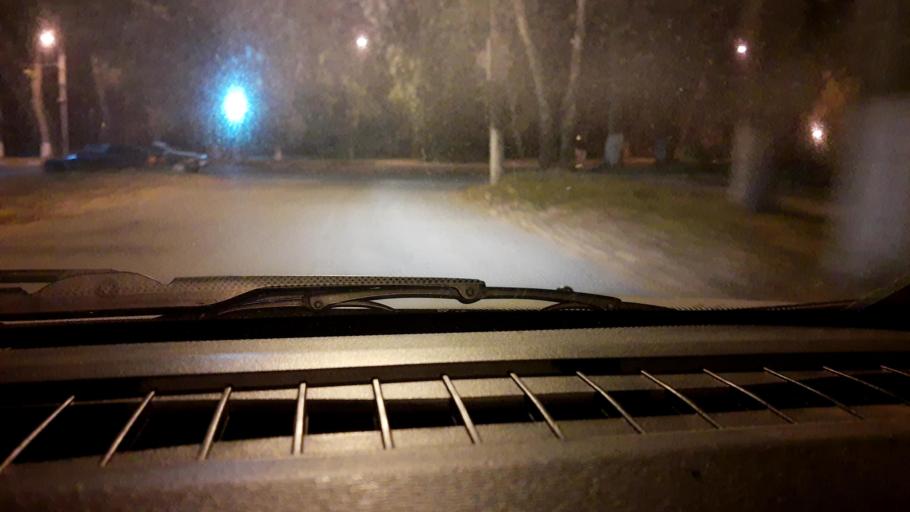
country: RU
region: Nizjnij Novgorod
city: Nizhniy Novgorod
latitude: 56.2408
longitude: 43.9572
